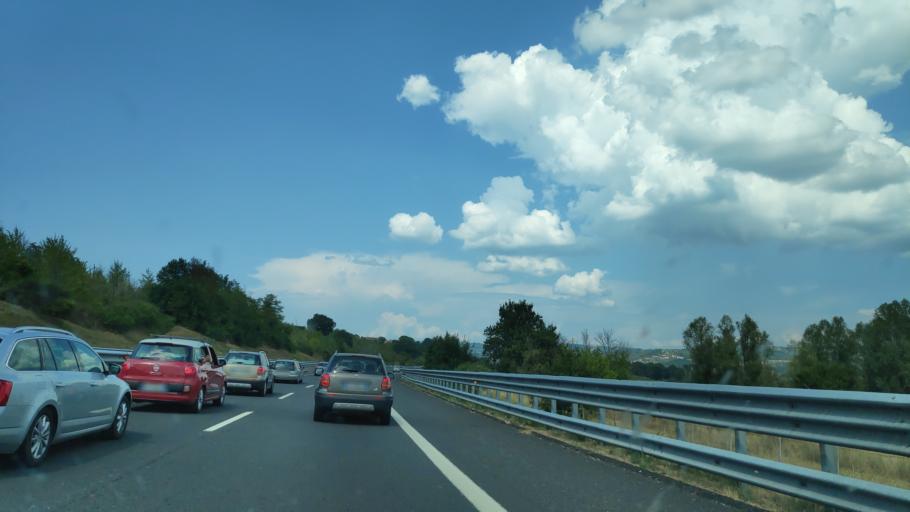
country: IT
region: Umbria
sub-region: Provincia di Terni
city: Fabro Scalo
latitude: 42.8503
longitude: 12.0377
